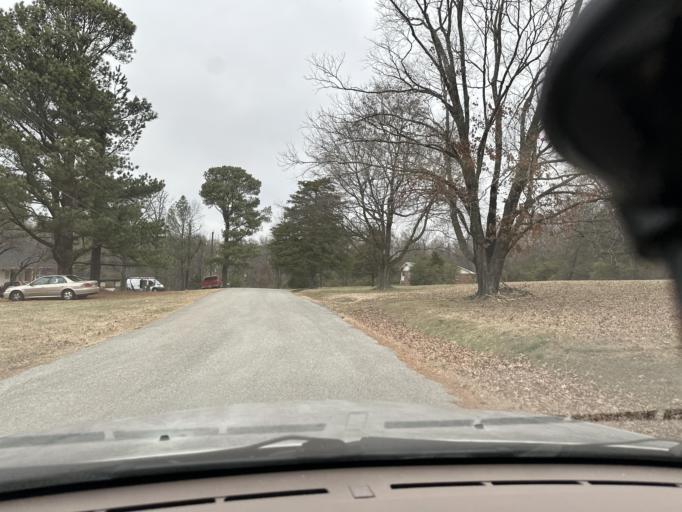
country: US
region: Arkansas
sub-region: Washington County
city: Fayetteville
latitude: 36.0894
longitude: -94.1197
